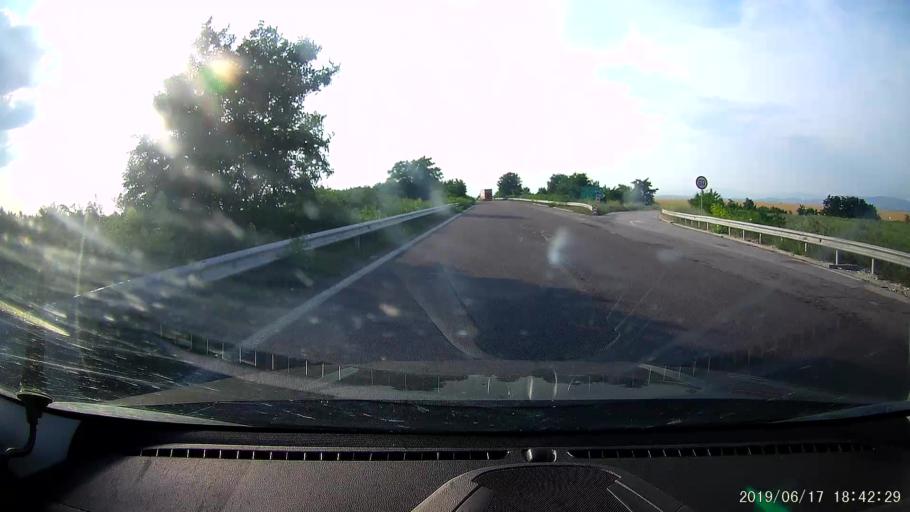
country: BG
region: Stara Zagora
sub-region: Obshtina Chirpan
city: Chirpan
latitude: 42.1921
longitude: 25.2362
